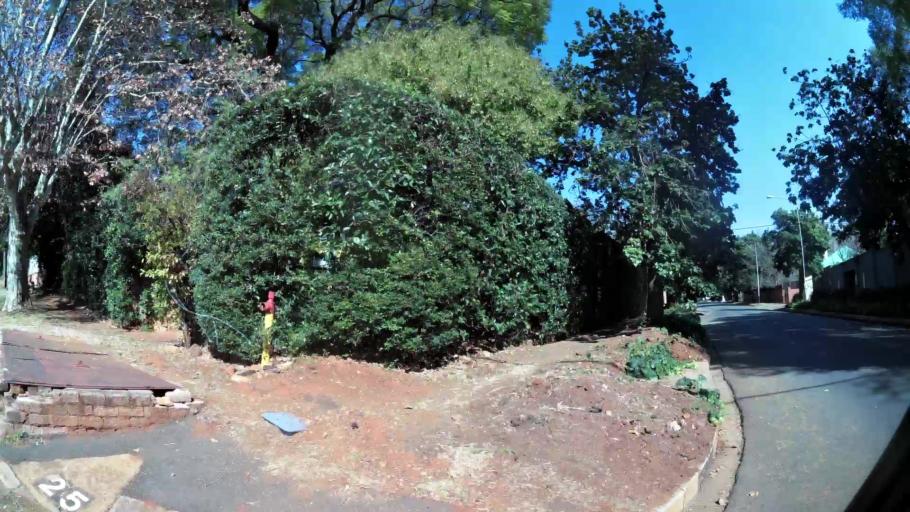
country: ZA
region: Gauteng
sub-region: City of Johannesburg Metropolitan Municipality
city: Johannesburg
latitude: -26.1637
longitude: 28.0304
